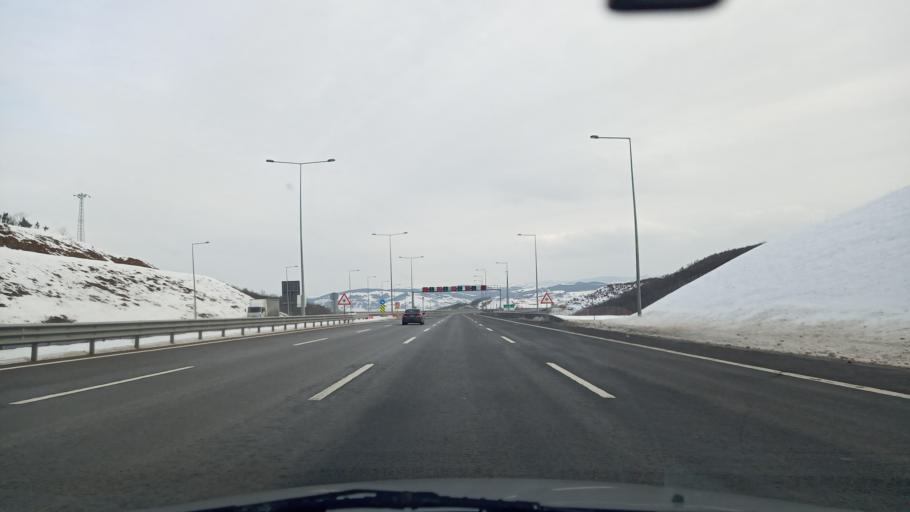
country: TR
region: Kocaeli
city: Korfez
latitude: 40.8893
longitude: 29.7246
